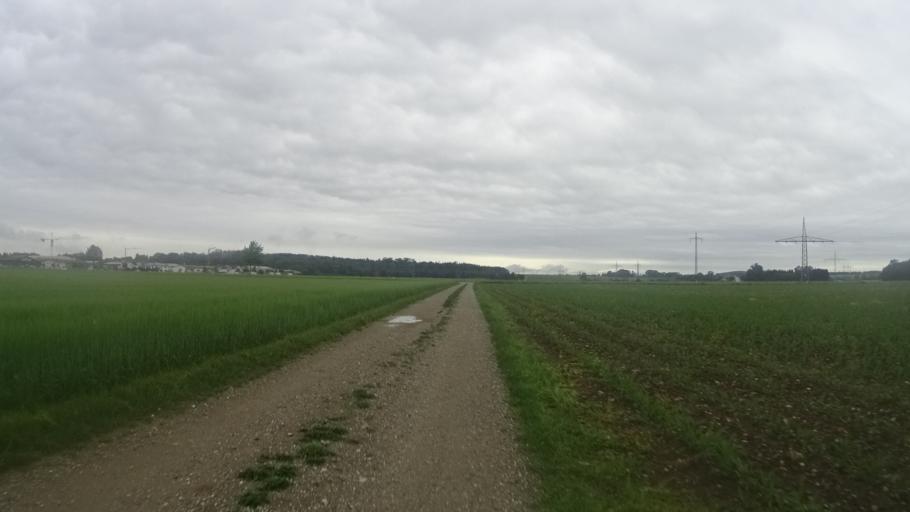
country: DE
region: Bavaria
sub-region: Upper Bavaria
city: Mammendorf
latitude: 48.2097
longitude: 11.1874
